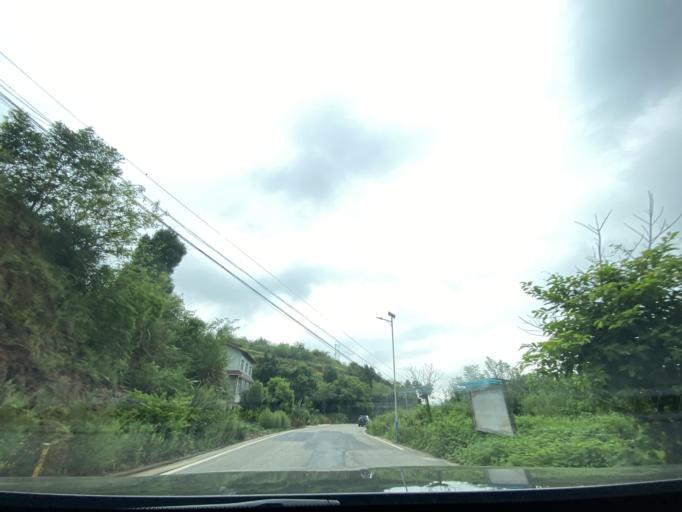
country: CN
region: Sichuan
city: Jiancheng
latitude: 30.5387
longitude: 104.5252
